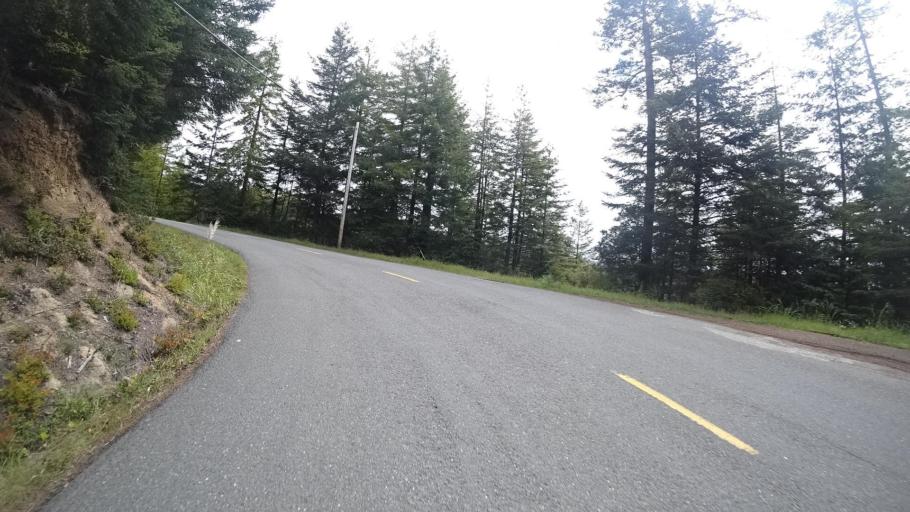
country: US
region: California
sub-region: Humboldt County
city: Bayside
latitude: 40.7856
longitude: -124.0683
